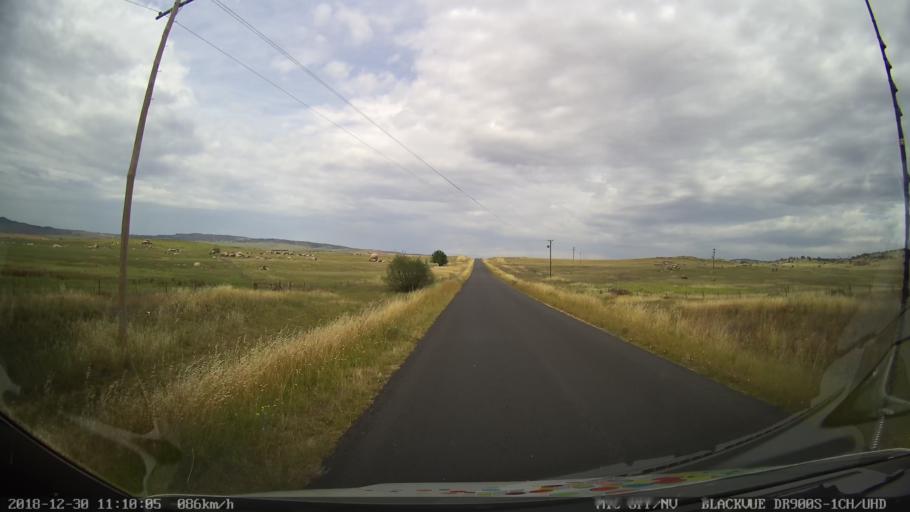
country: AU
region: New South Wales
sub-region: Snowy River
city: Berridale
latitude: -36.5115
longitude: 148.7855
